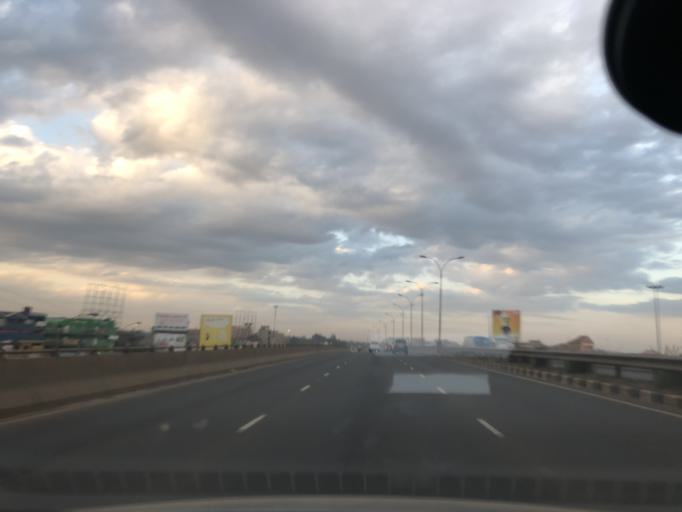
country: KE
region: Kiambu
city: Kiambu
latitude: -1.2048
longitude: 36.9160
